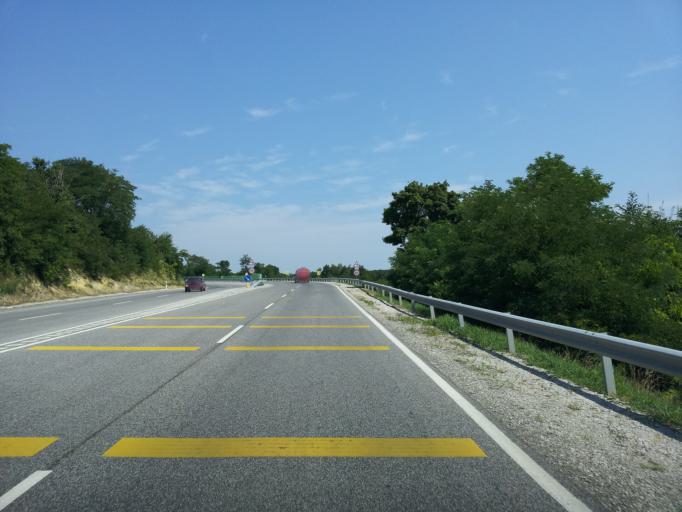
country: HU
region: Zala
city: Pacsa
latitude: 46.8276
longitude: 16.9719
